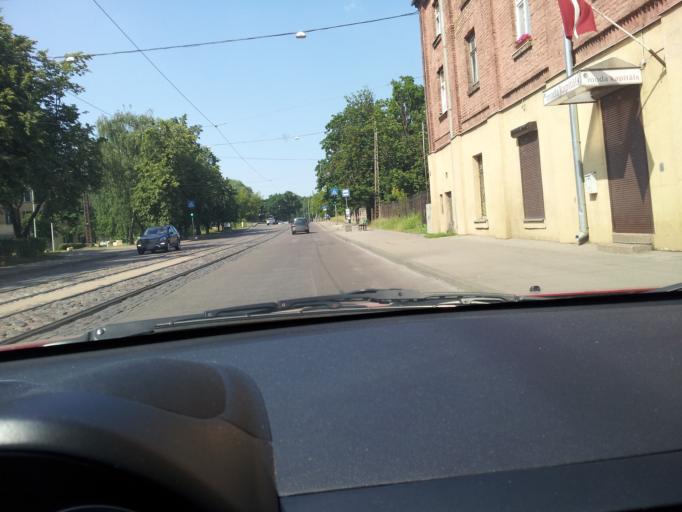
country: LV
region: Riga
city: Riga
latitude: 56.9907
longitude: 24.1222
